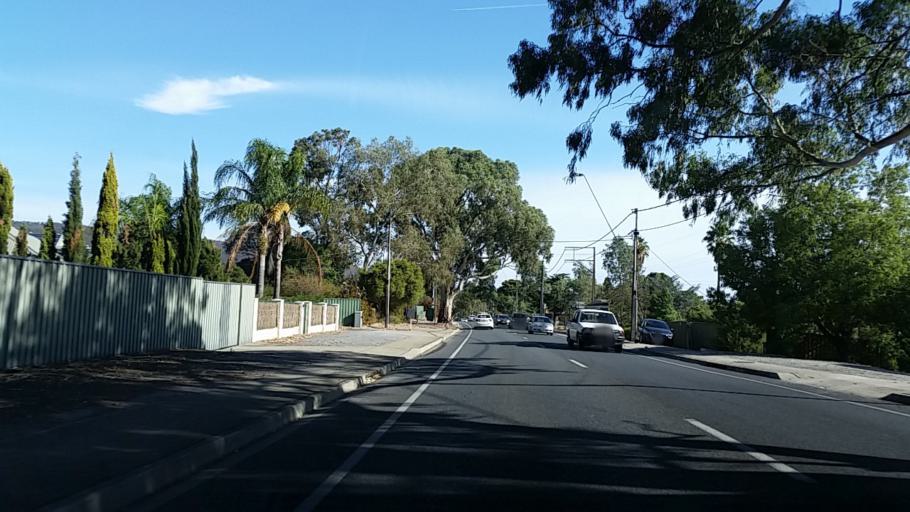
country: AU
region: South Australia
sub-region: Tea Tree Gully
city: Hope Valley
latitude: -34.8452
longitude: 138.7175
